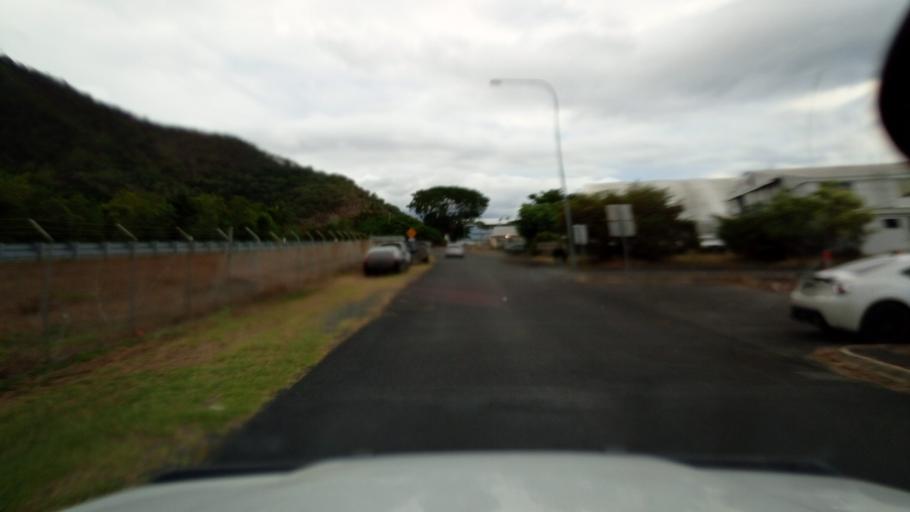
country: AU
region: Queensland
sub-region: Cairns
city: Cairns
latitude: -16.8876
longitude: 145.7510
